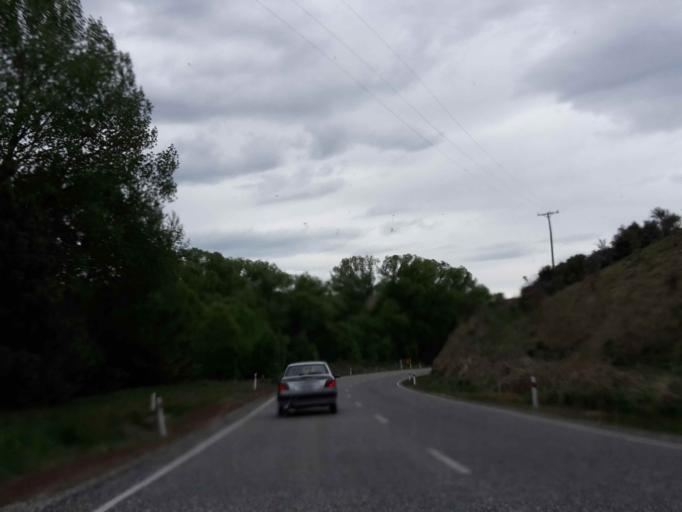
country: NZ
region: Otago
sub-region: Queenstown-Lakes District
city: Wanaka
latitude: -44.7171
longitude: 169.5046
